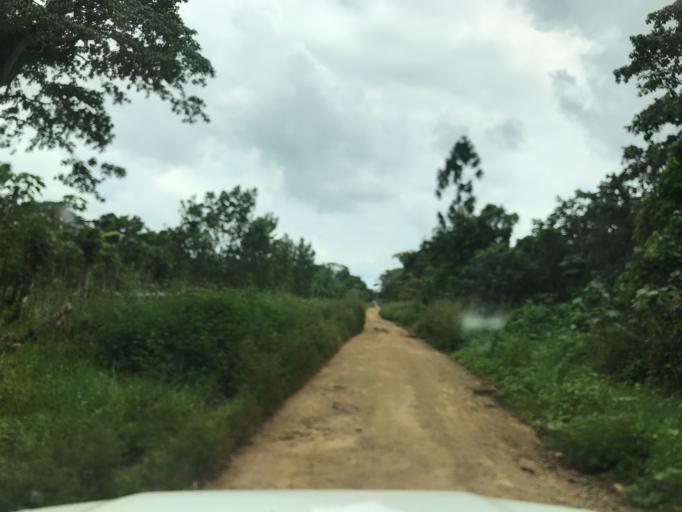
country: VU
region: Sanma
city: Port-Olry
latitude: -15.1848
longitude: 167.0299
